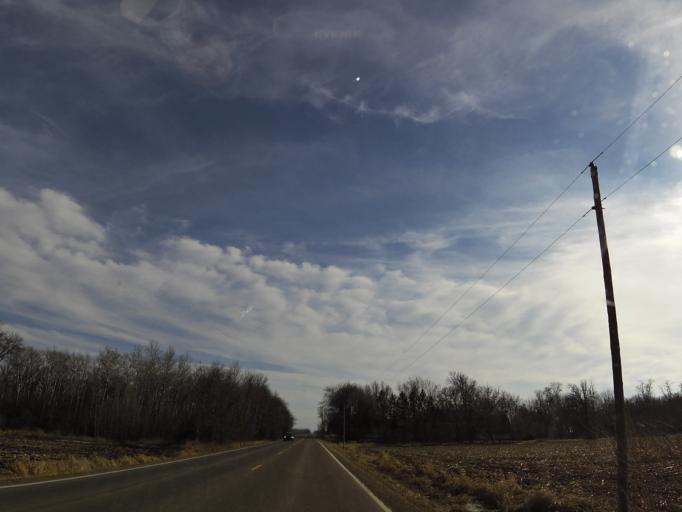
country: US
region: Minnesota
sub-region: Rice County
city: Northfield
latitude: 44.5186
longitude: -93.2007
